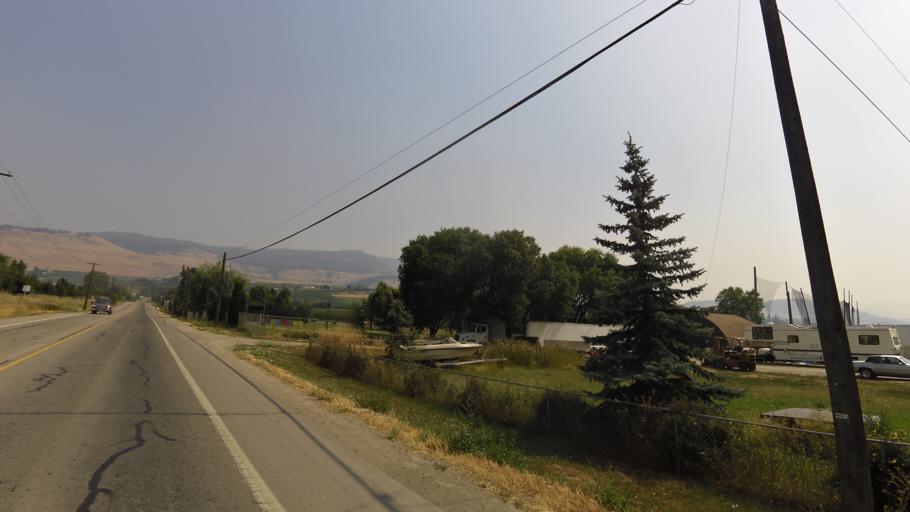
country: CA
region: British Columbia
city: Kelowna
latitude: 49.9181
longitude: -119.3776
